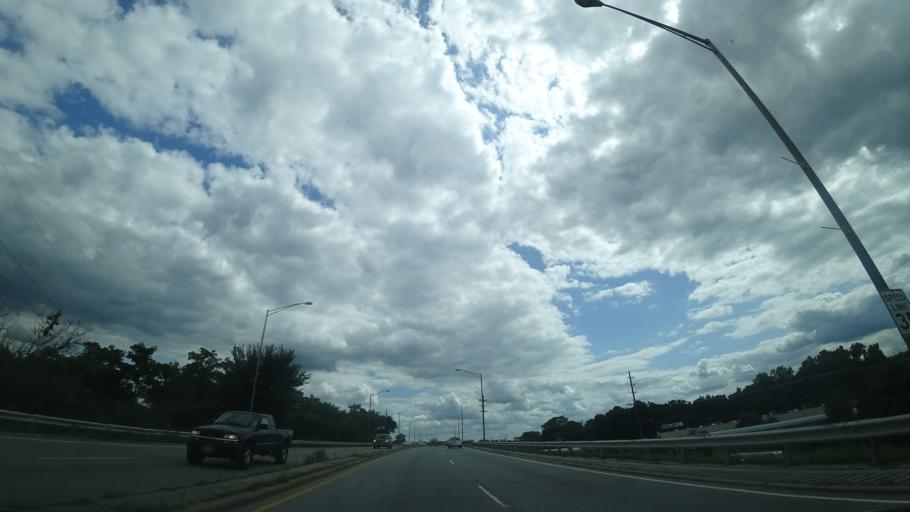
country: US
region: Illinois
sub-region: Cook County
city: Alsip
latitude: 41.6802
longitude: -87.7390
